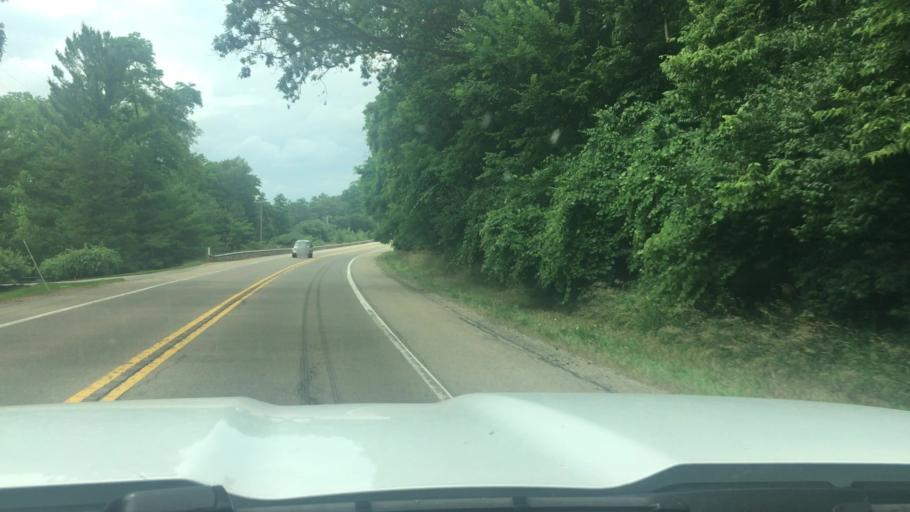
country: US
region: Michigan
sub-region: Kent County
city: Forest Hills
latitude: 42.9394
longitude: -85.4496
